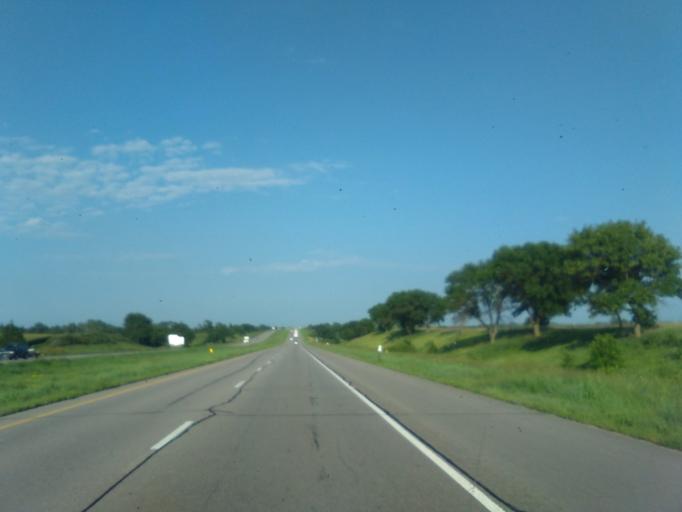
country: US
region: Nebraska
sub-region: Saline County
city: Friend
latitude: 40.8222
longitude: -97.2704
